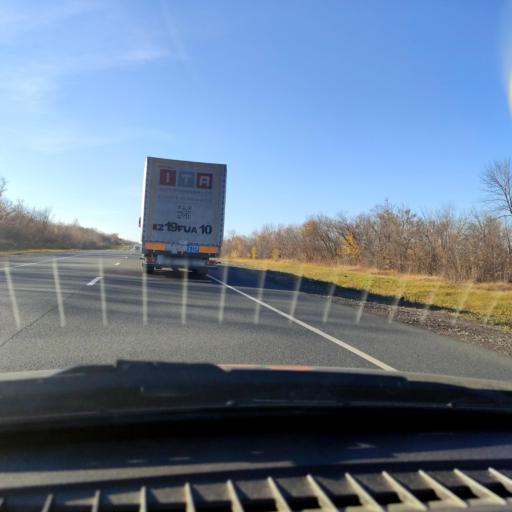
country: RU
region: Samara
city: Mezhdurechensk
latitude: 53.2572
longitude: 49.1162
